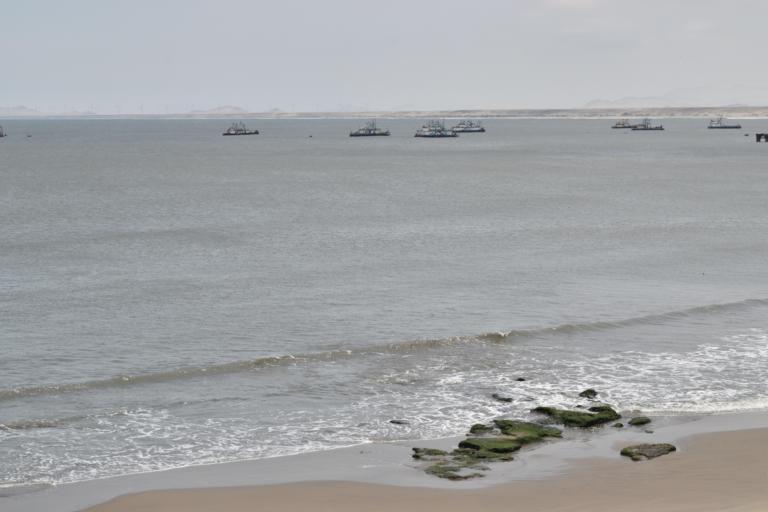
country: PE
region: La Libertad
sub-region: Ascope
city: Paijan
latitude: -7.7039
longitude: -79.4434
